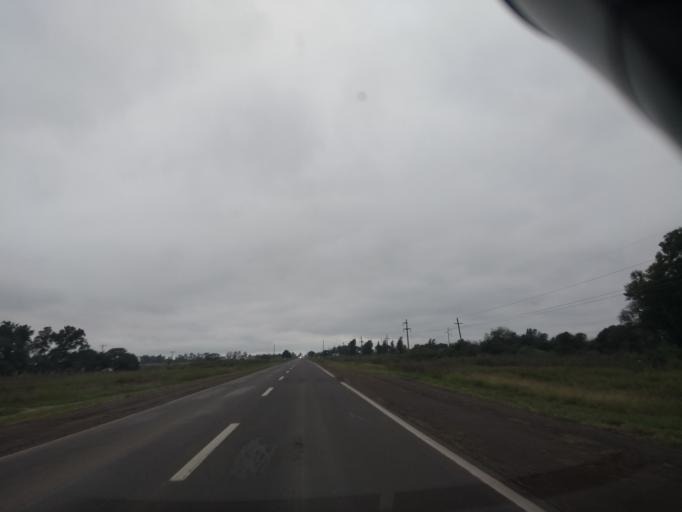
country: AR
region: Chaco
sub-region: Departamento de Quitilipi
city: Quitilipi
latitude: -26.8704
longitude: -60.2550
